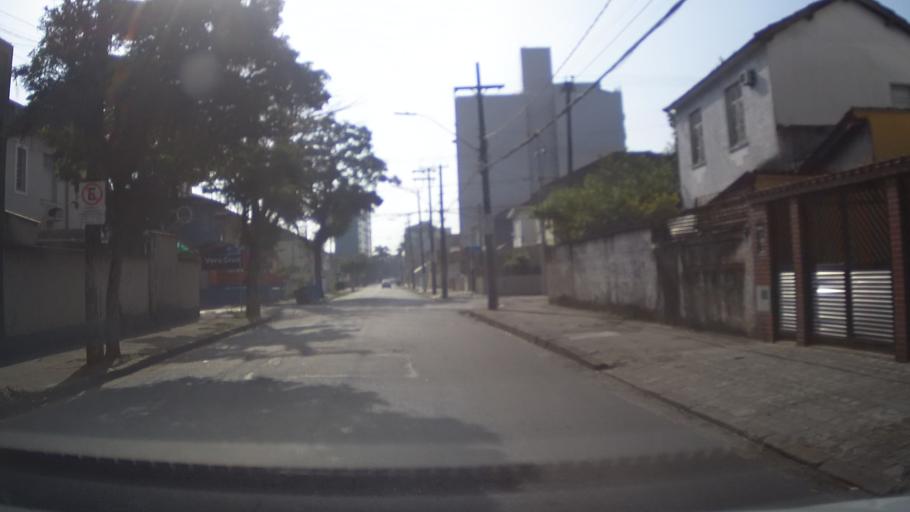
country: BR
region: Sao Paulo
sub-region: Santos
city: Santos
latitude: -23.9461
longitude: -46.3332
